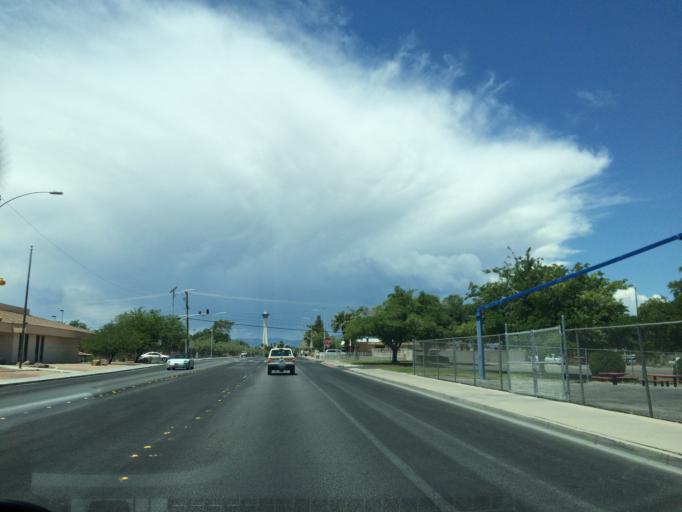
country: US
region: Nevada
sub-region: Clark County
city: Winchester
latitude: 36.1481
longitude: -115.1133
